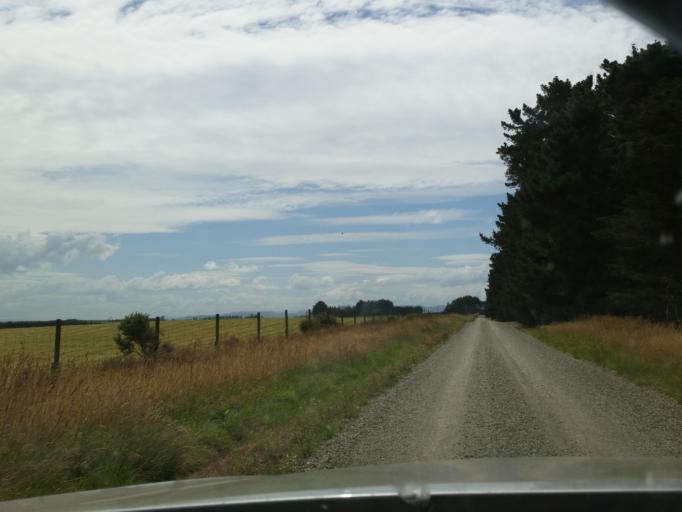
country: NZ
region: Southland
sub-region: Southland District
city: Winton
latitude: -46.2046
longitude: 168.4869
